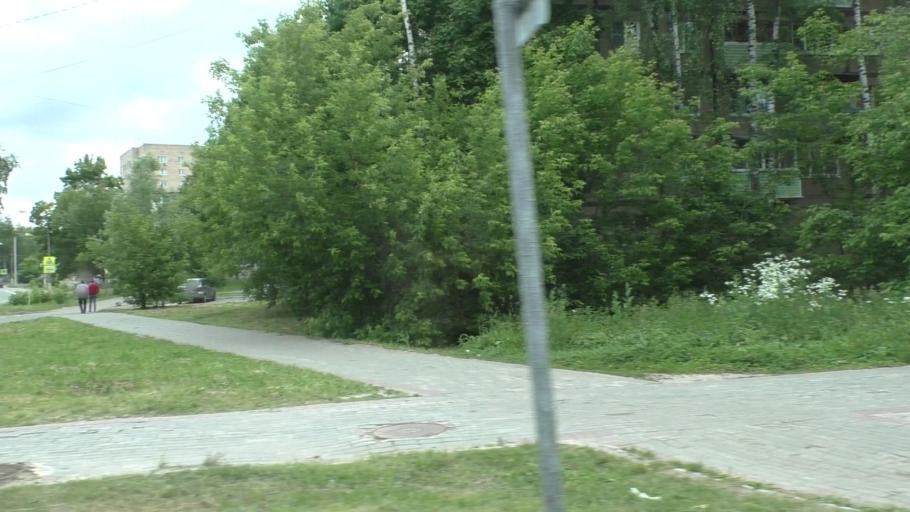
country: RU
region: Moskovskaya
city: Yegor'yevsk
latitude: 55.3698
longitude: 39.0526
